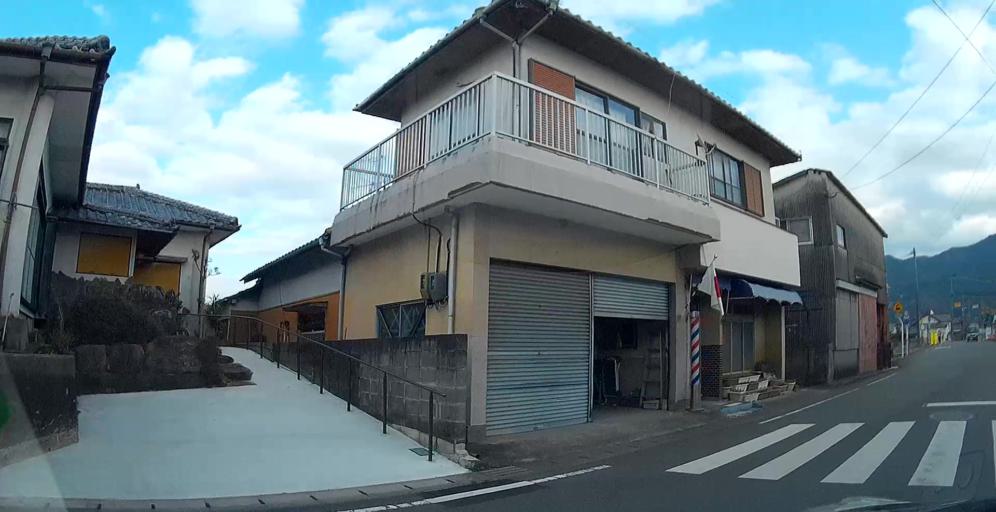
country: JP
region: Kumamoto
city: Yatsushiro
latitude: 32.5358
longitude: 130.6471
